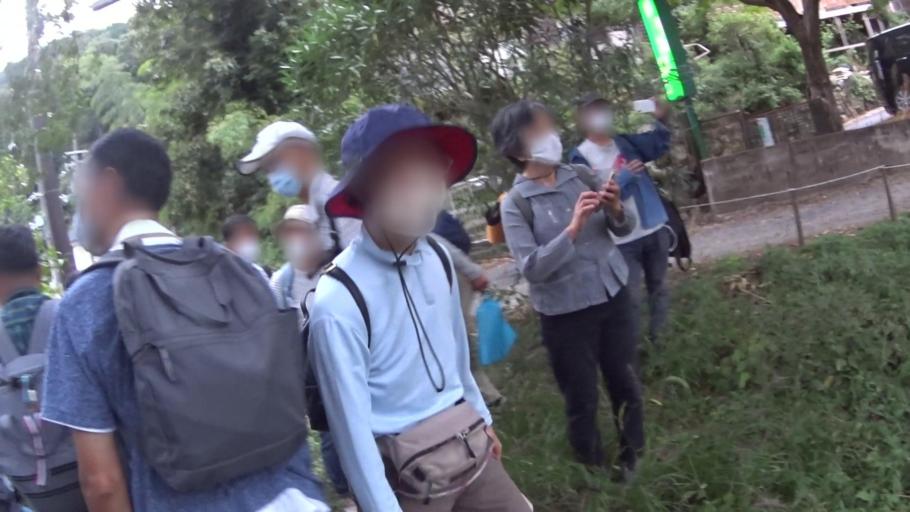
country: JP
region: Osaka
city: Kaizuka
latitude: 34.4490
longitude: 135.2816
